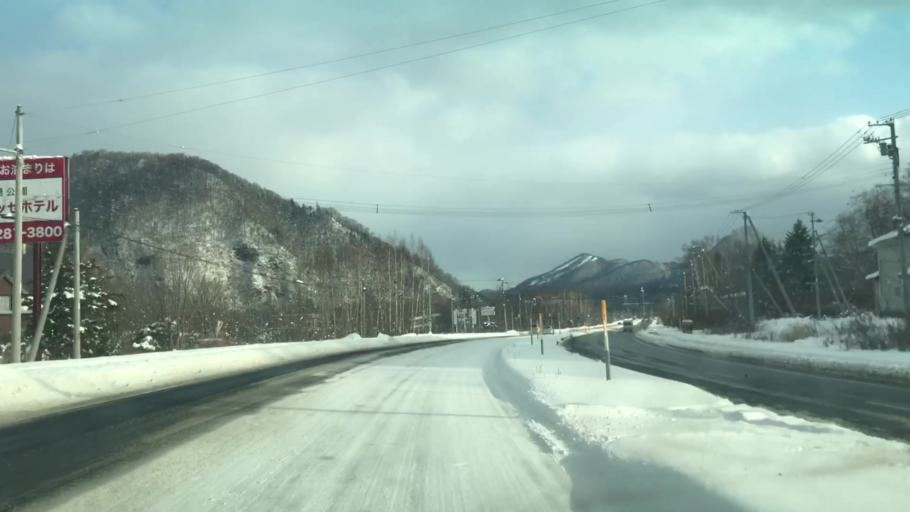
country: JP
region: Hokkaido
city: Sapporo
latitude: 42.9695
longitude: 141.2105
